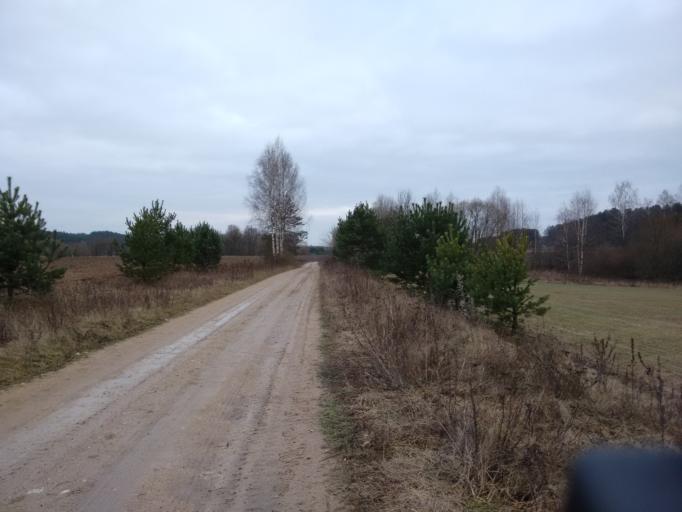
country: LT
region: Alytaus apskritis
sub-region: Alytus
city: Alytus
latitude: 54.2312
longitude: 23.9601
